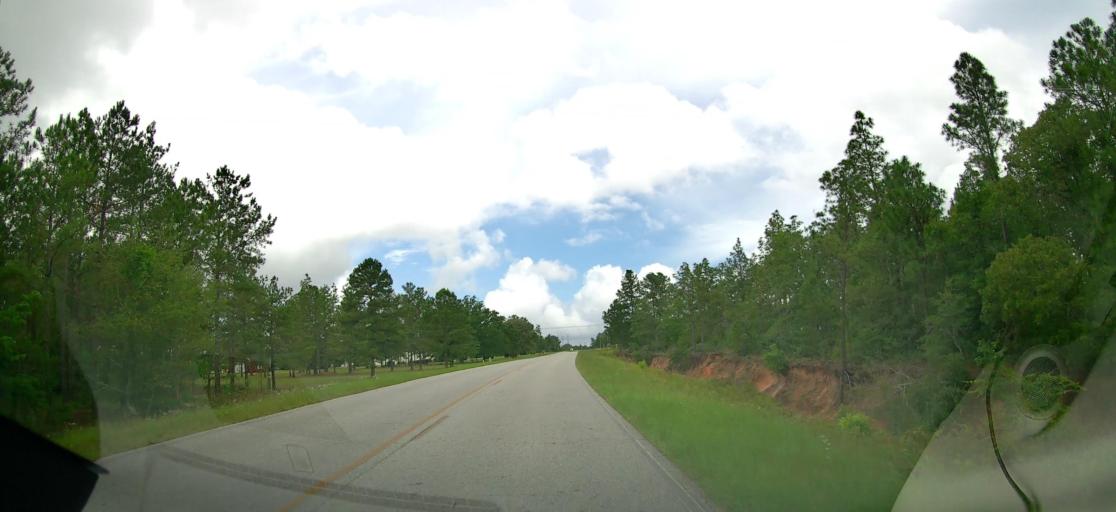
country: US
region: Georgia
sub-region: Peach County
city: Byron
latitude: 32.6927
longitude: -83.7716
